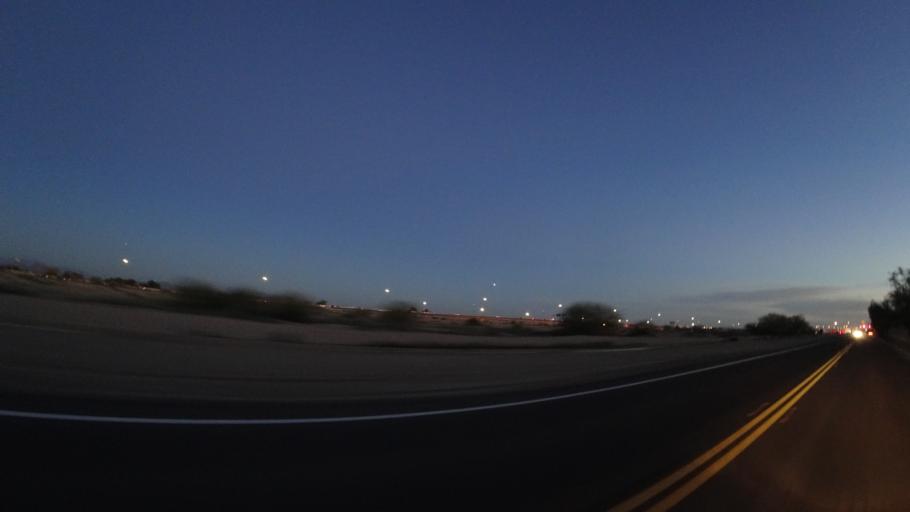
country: US
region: Arizona
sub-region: Maricopa County
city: Scottsdale
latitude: 33.4700
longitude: -111.8920
